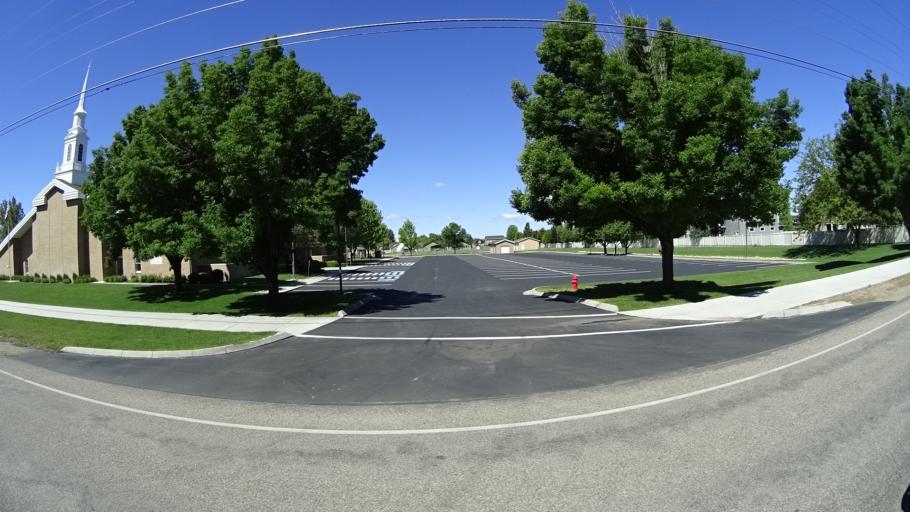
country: US
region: Idaho
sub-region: Ada County
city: Eagle
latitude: 43.6552
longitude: -116.3745
